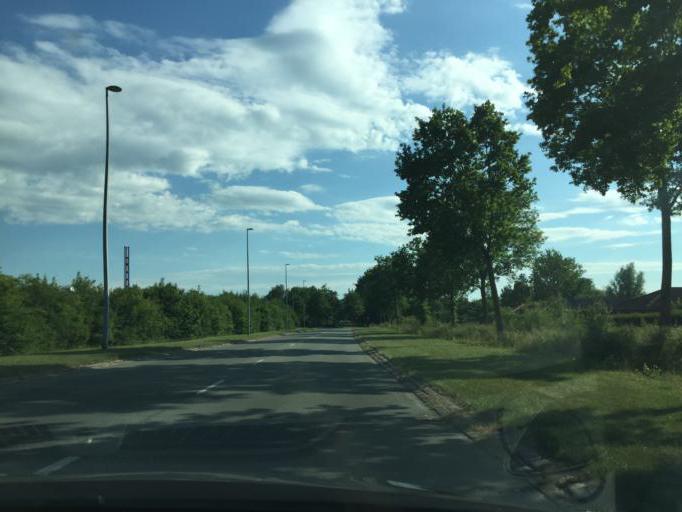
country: DK
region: South Denmark
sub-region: Odense Kommune
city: Neder Holluf
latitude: 55.3722
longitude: 10.4579
